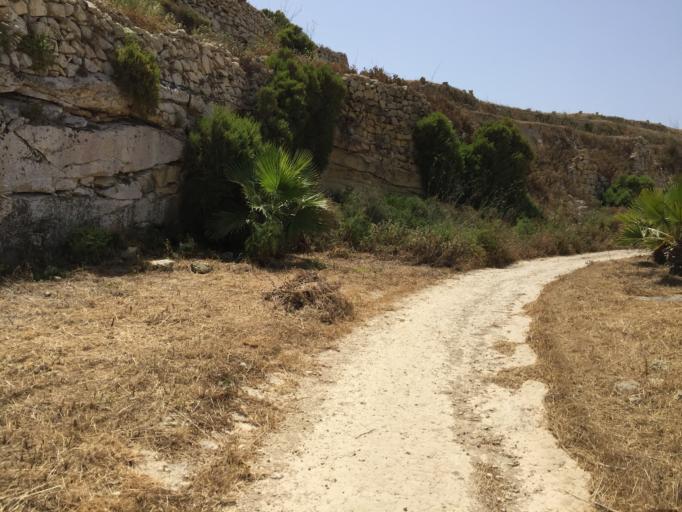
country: MT
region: Il-Munxar
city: Munxar
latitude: 36.0251
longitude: 14.2188
